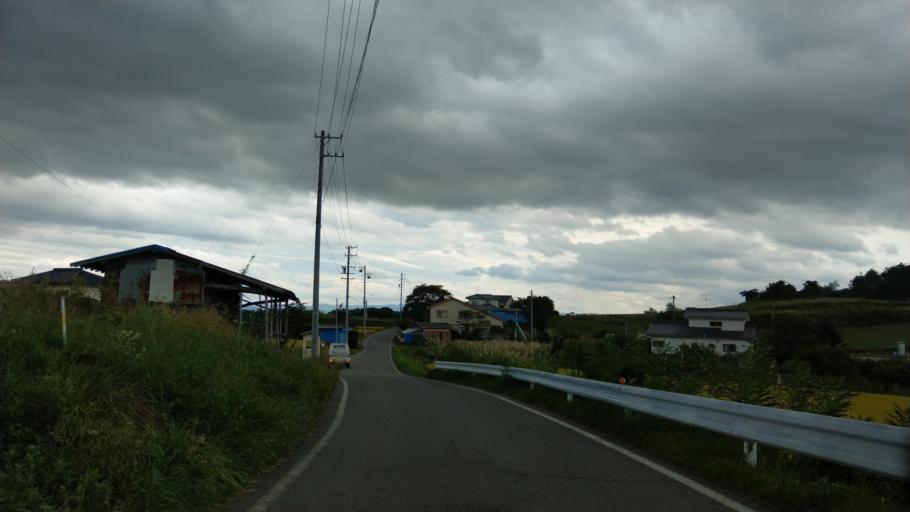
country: JP
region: Nagano
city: Komoro
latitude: 36.3145
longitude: 138.3918
